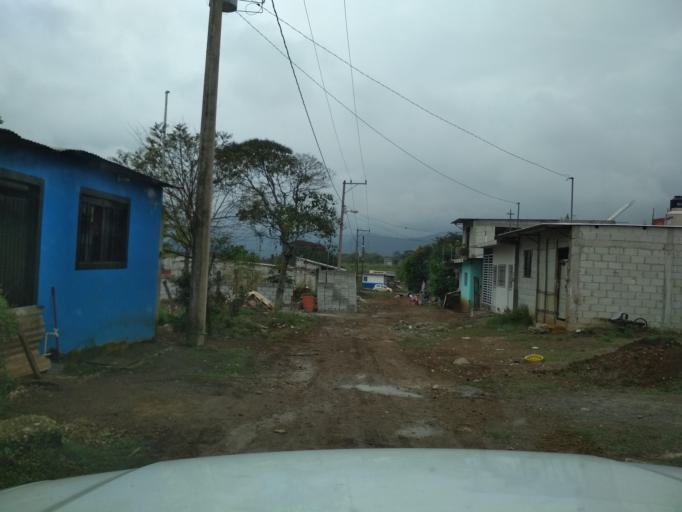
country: MX
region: Veracruz
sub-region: Cordoba
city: San Jose de Tapia
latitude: 18.8452
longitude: -96.9661
